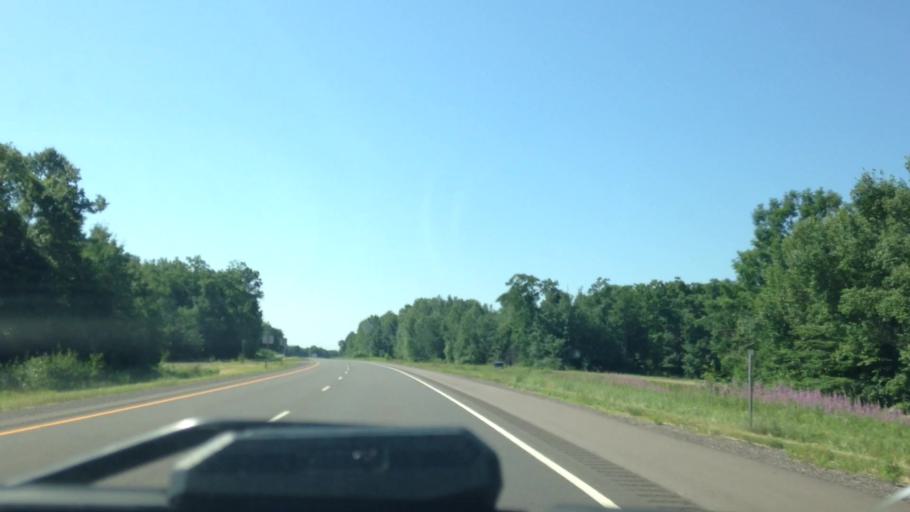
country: US
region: Wisconsin
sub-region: Washburn County
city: Spooner
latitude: 45.9437
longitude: -91.8293
